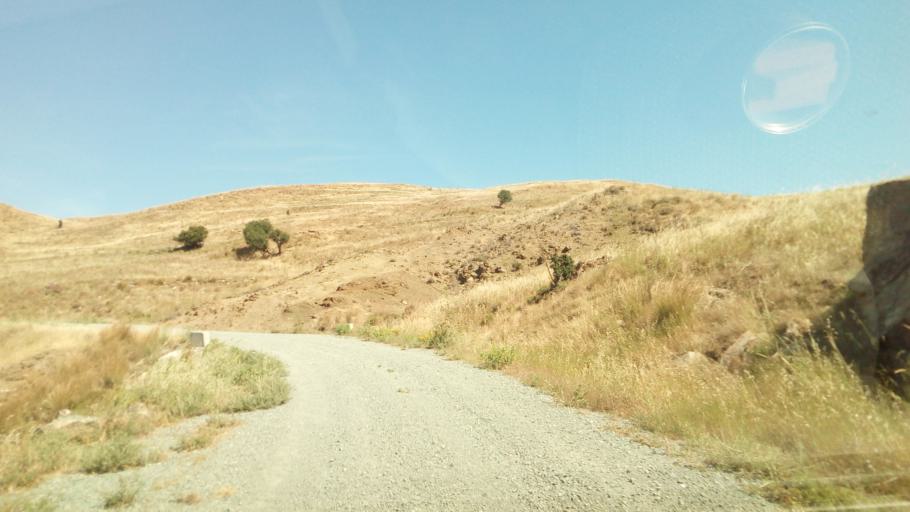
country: CY
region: Limassol
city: Pachna
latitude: 34.8151
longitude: 32.7085
